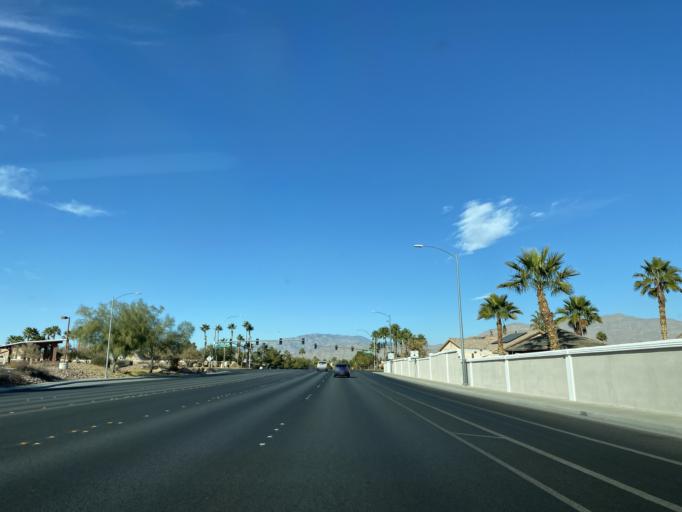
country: US
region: Nevada
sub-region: Clark County
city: Las Vegas
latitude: 36.2894
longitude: -115.2602
